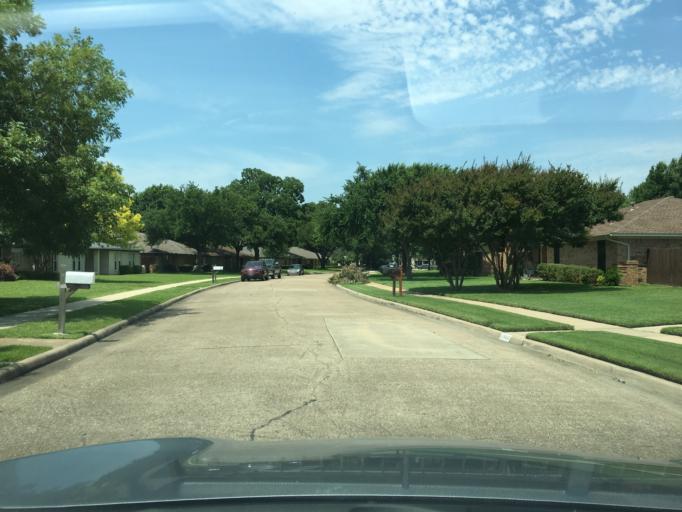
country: US
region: Texas
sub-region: Dallas County
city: Richardson
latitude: 32.9653
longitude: -96.6978
